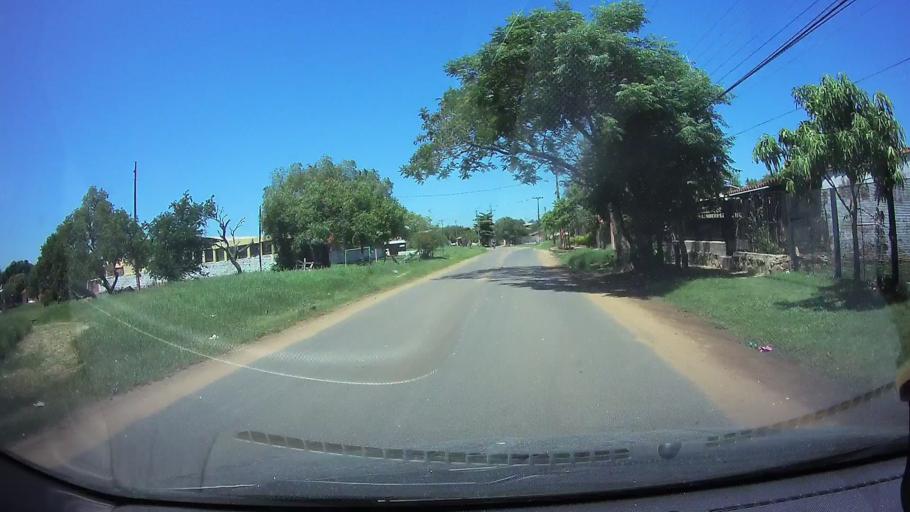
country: PY
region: Central
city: San Lorenzo
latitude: -25.3256
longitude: -57.4840
